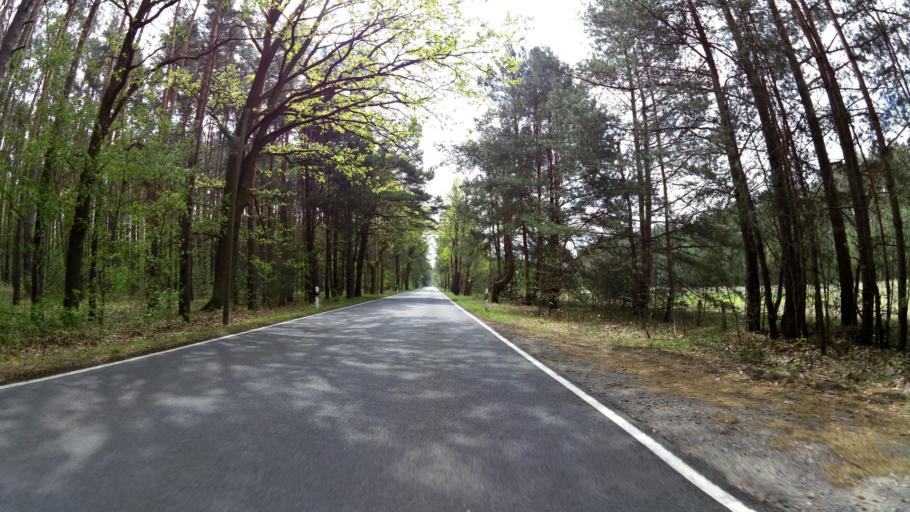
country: DE
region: Brandenburg
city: Bestensee
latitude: 52.2768
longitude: 13.7337
